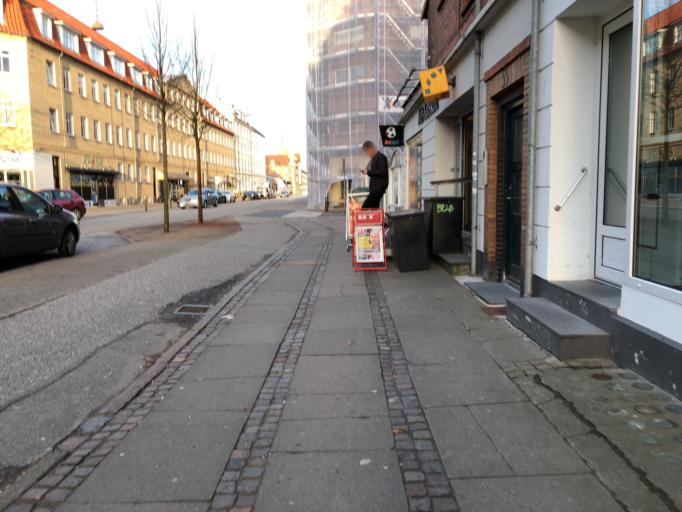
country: DK
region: North Denmark
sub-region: Alborg Kommune
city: Aalborg
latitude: 57.0538
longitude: 9.9024
